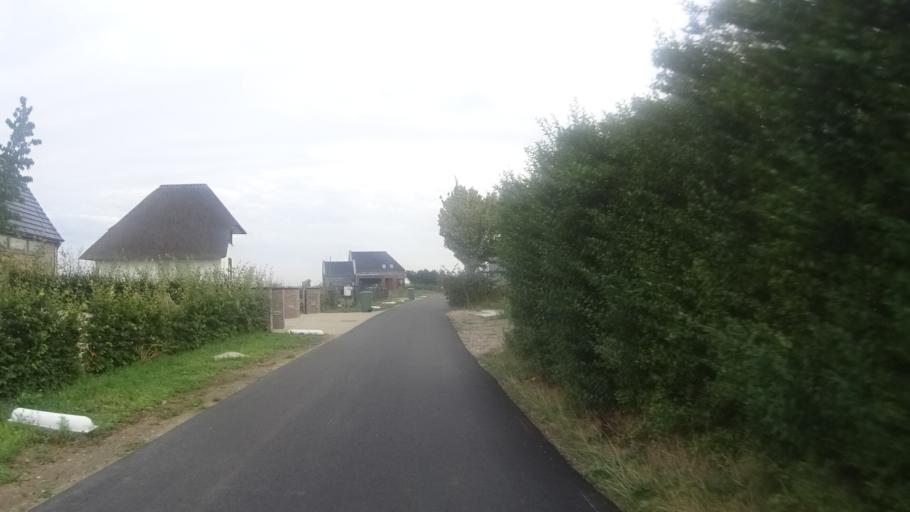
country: NL
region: Limburg
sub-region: Gemeente Venlo
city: Arcen
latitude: 51.4327
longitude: 6.1625
